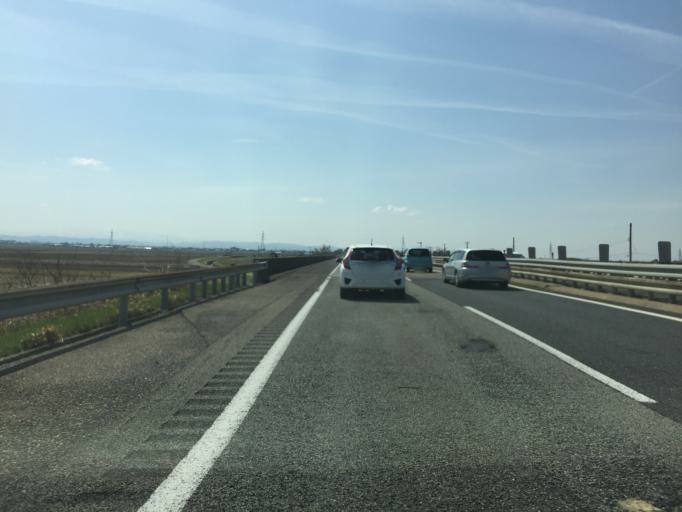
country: JP
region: Niigata
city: Tsubame
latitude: 37.7109
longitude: 138.9399
